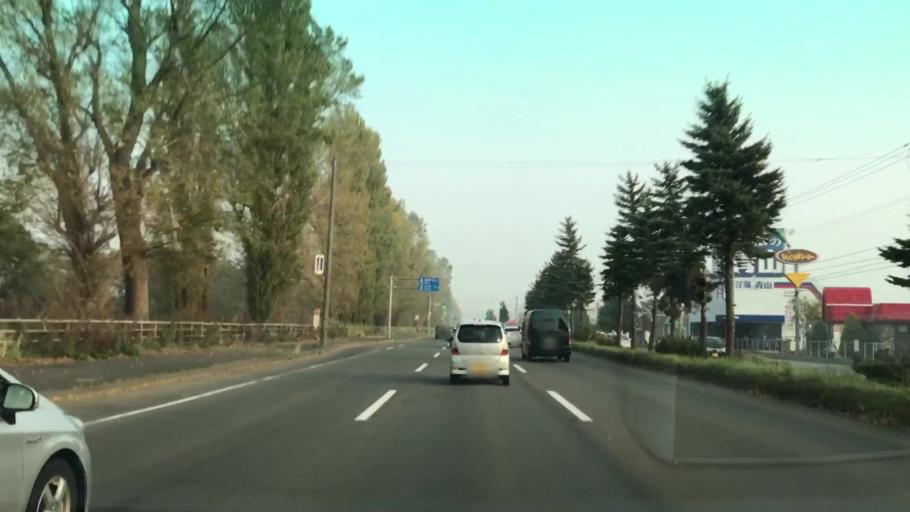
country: JP
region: Hokkaido
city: Sapporo
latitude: 43.1358
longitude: 141.3475
